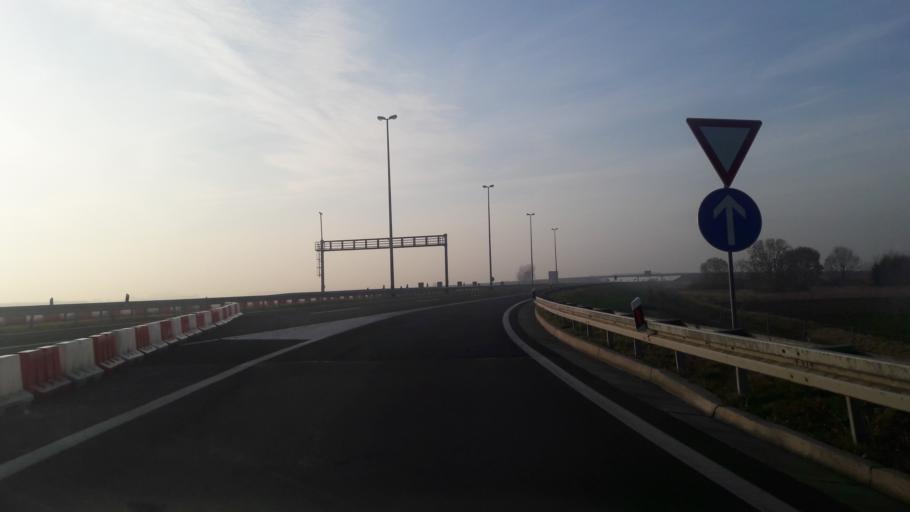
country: HR
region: Osjecko-Baranjska
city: Josipovac
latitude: 45.5728
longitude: 18.5508
